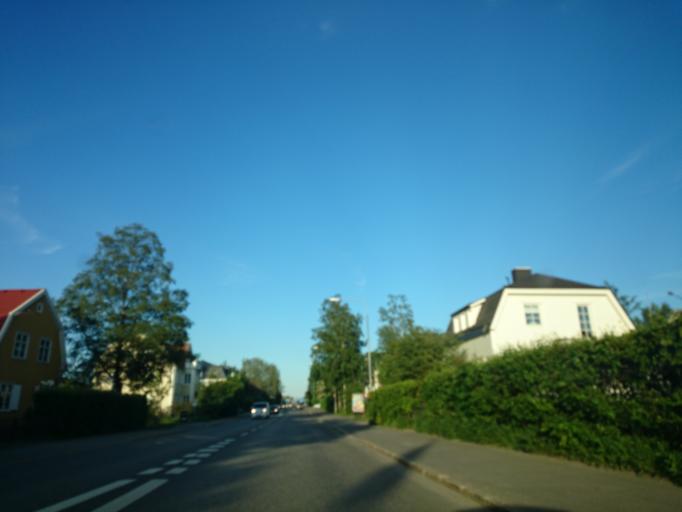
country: SE
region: Vaesternorrland
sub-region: Sundsvalls Kommun
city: Sundsvall
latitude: 62.3880
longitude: 17.2873
